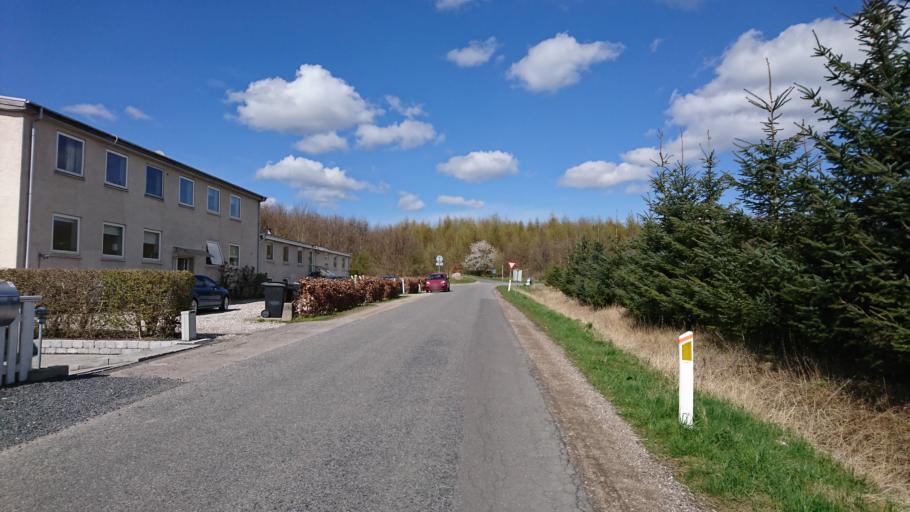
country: DK
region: Capital Region
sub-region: Egedal Kommune
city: Ganlose
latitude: 55.7786
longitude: 12.2652
